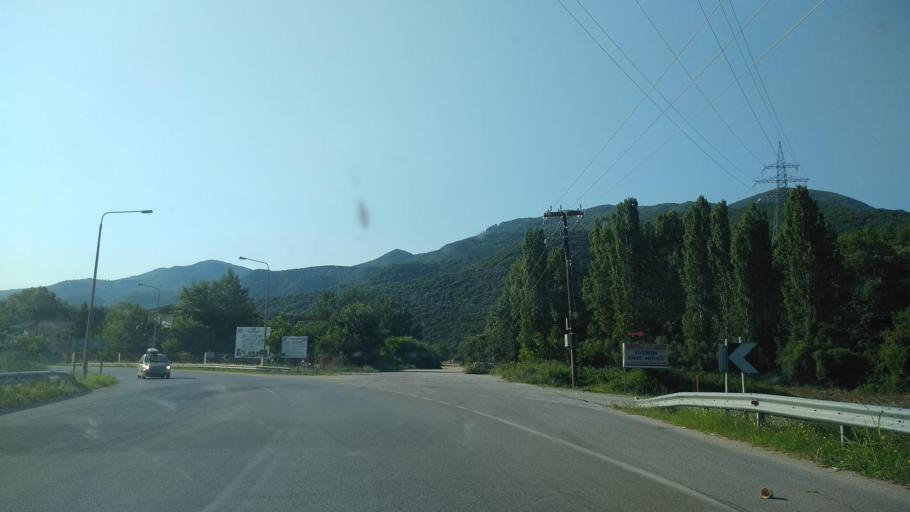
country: GR
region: Central Macedonia
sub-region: Nomos Thessalonikis
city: Stavros
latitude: 40.6713
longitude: 23.6638
